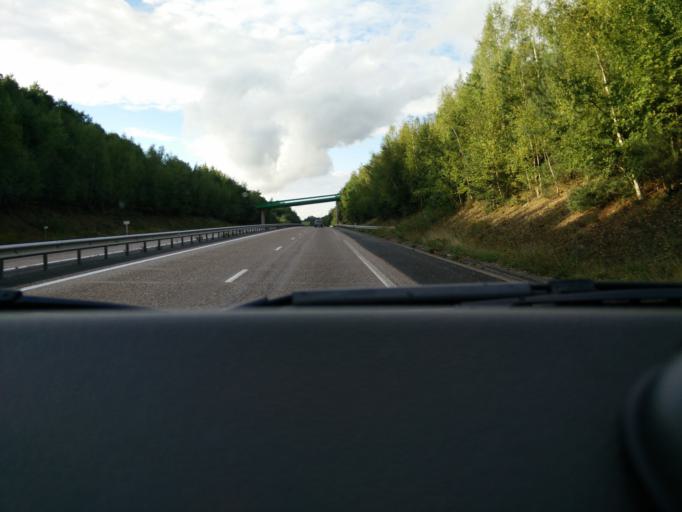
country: FR
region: Lorraine
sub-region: Departement de Meurthe-et-Moselle
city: Baccarat
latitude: 48.4526
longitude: 6.7524
